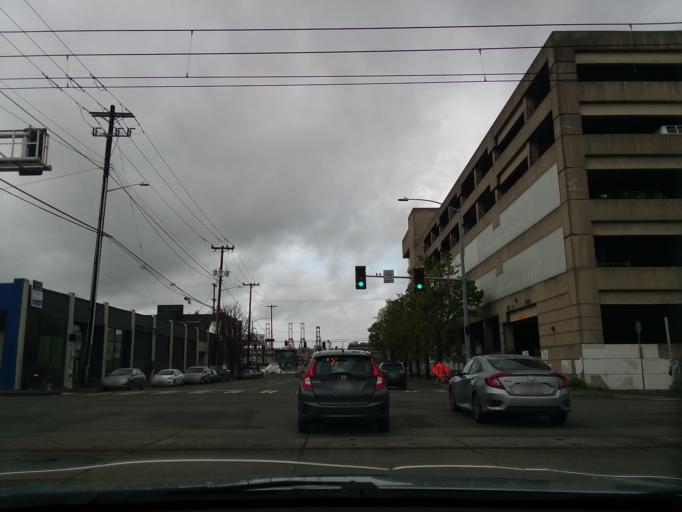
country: US
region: Washington
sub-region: King County
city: Seattle
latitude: 47.5798
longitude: -122.3273
